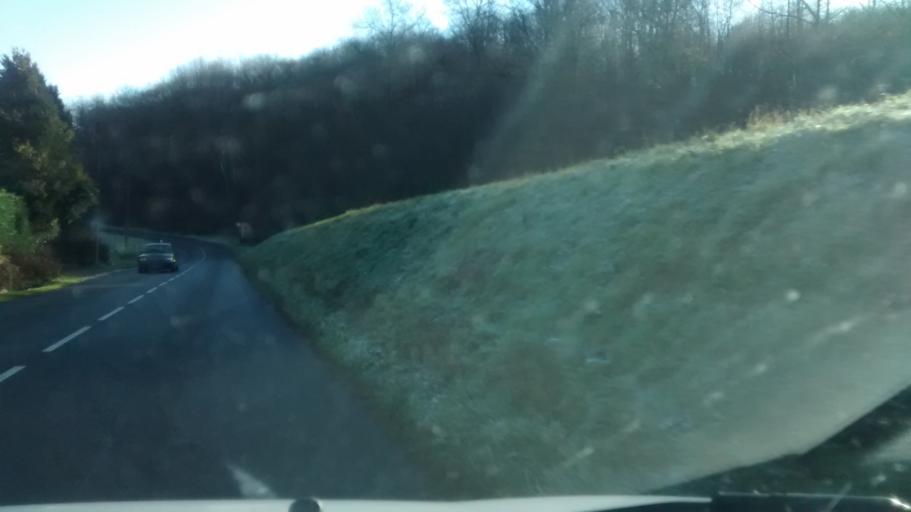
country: FR
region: Centre
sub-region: Departement d'Indre-et-Loire
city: Reugny
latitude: 47.4824
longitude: 0.8742
